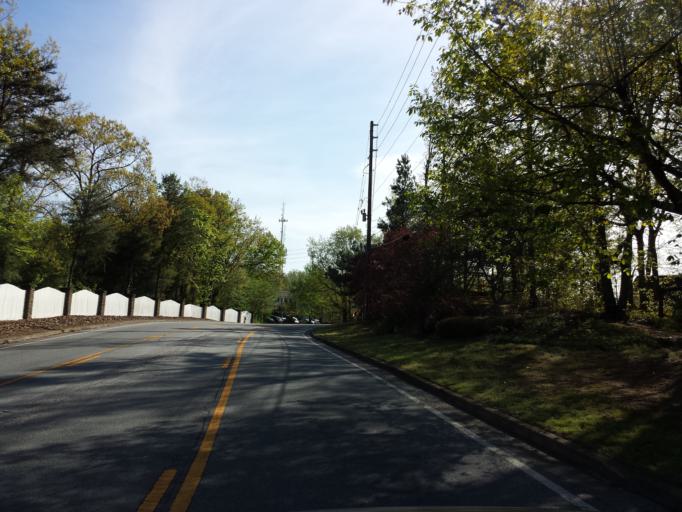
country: US
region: Georgia
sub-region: Cobb County
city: Marietta
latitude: 33.9759
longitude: -84.4989
